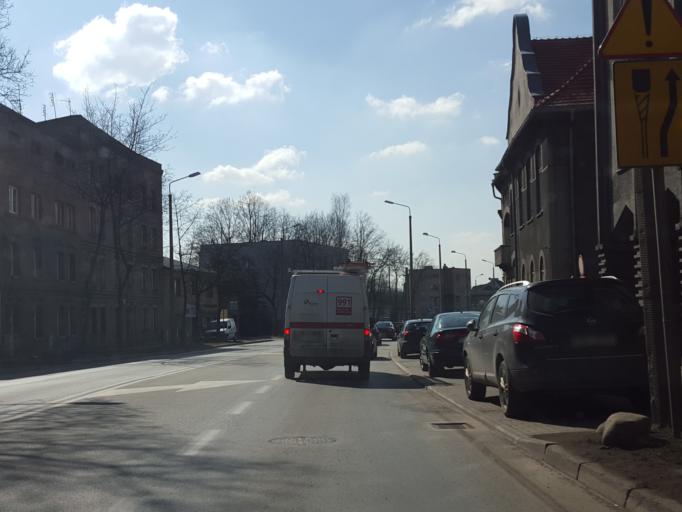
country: PL
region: Silesian Voivodeship
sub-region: Ruda Slaska
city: Ruda Slaska
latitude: 50.2655
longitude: 18.8619
